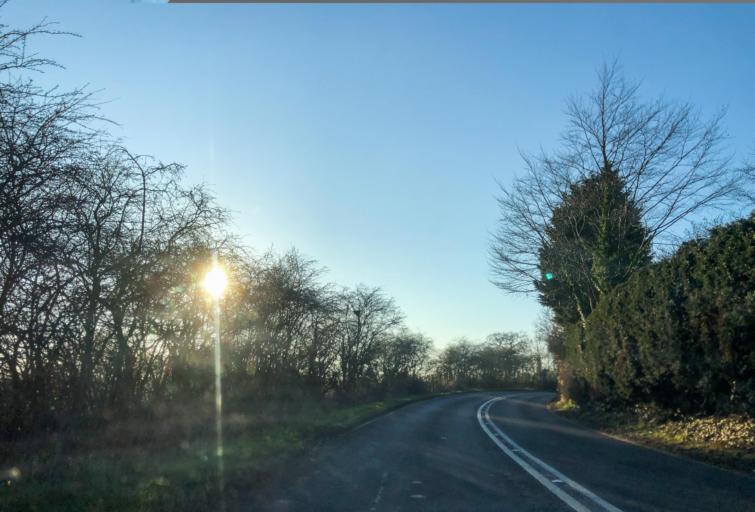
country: GB
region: England
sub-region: Warwickshire
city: Wroxall
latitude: 52.2735
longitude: -1.6585
